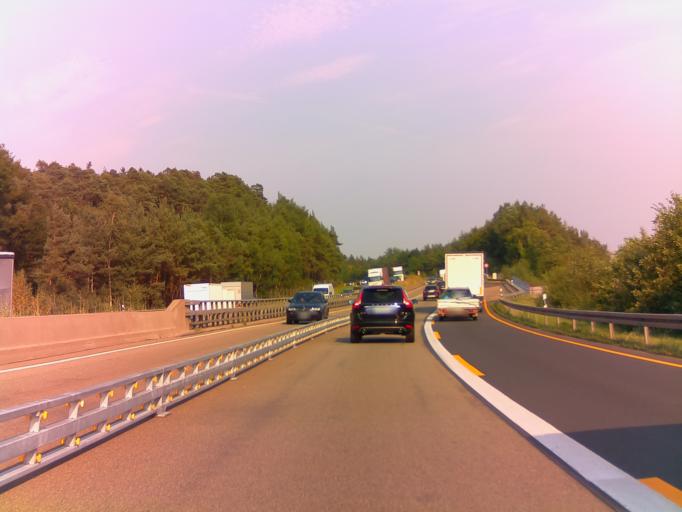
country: DE
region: Hesse
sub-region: Regierungsbezirk Kassel
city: Kirchheim
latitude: 50.8079
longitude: 9.5152
